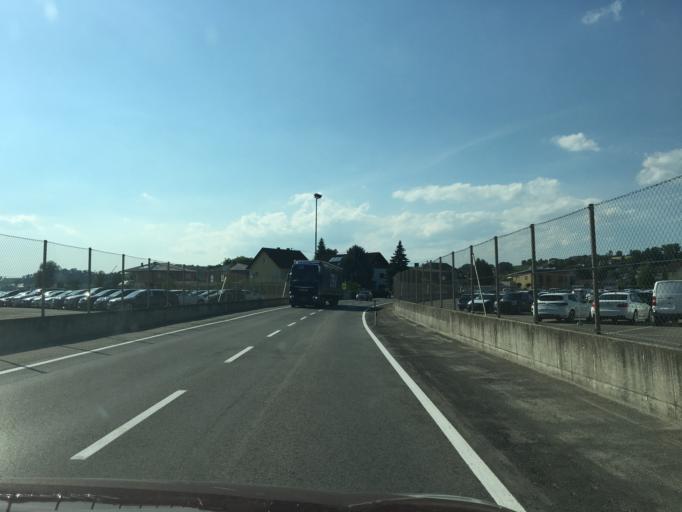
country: AT
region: Upper Austria
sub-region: Politischer Bezirk Perg
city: Perg
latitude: 48.2649
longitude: 14.5742
